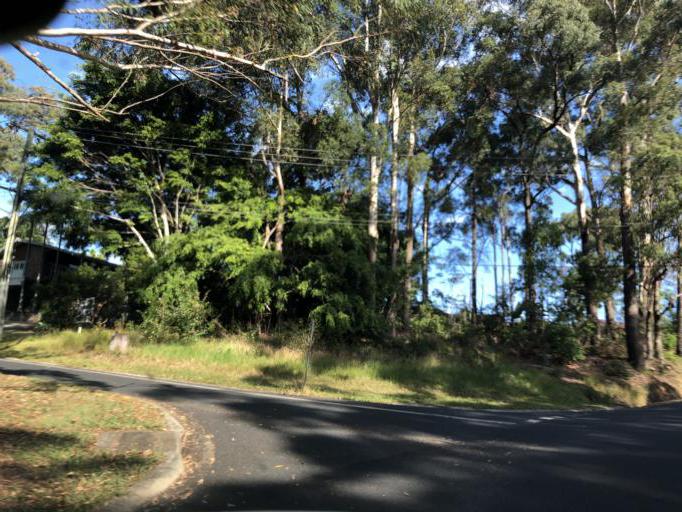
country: AU
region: New South Wales
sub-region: Coffs Harbour
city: Coffs Harbour
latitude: -30.2596
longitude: 153.1328
